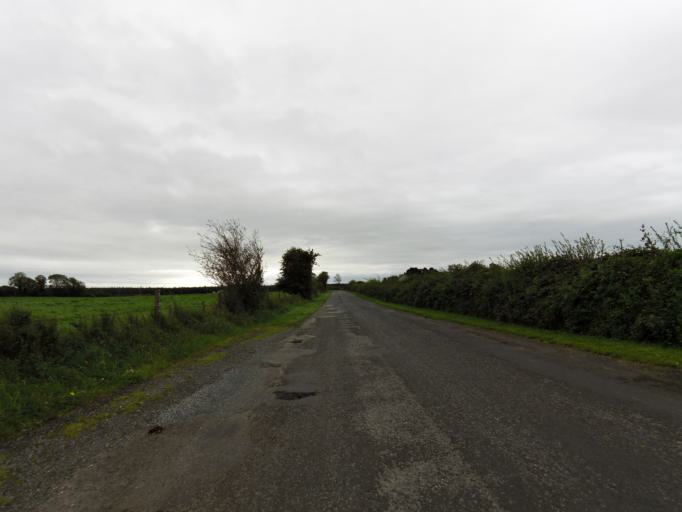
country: IE
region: Leinster
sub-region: Uibh Fhaili
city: Ferbane
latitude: 53.2339
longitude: -7.7312
